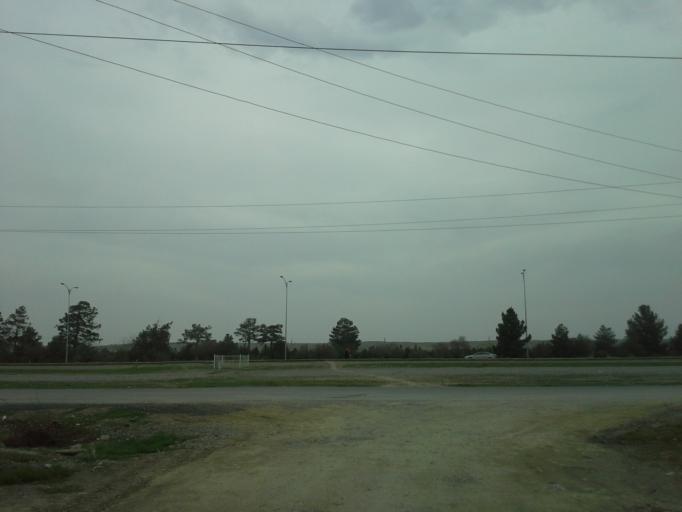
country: TM
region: Ahal
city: Abadan
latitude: 37.9690
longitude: 58.2295
